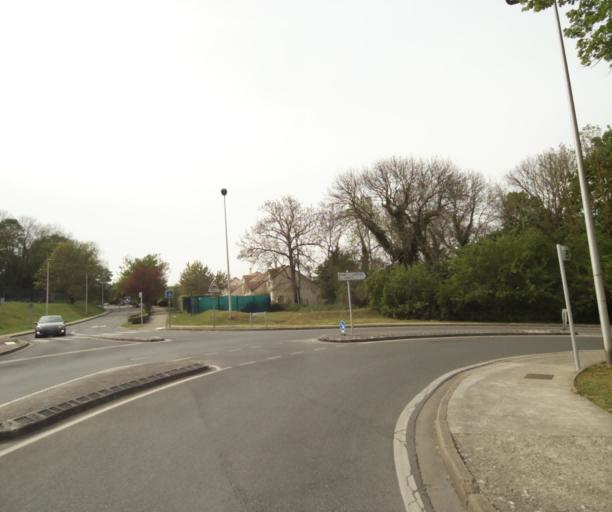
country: FR
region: Ile-de-France
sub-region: Departement de Seine-et-Marne
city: Torcy
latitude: 48.8555
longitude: 2.6554
